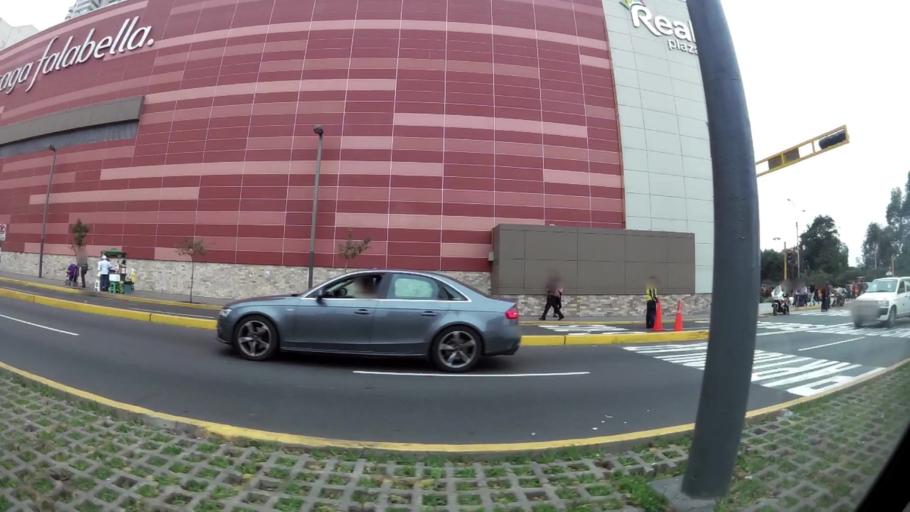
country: PE
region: Lima
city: Lima
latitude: -12.0575
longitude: -77.0380
